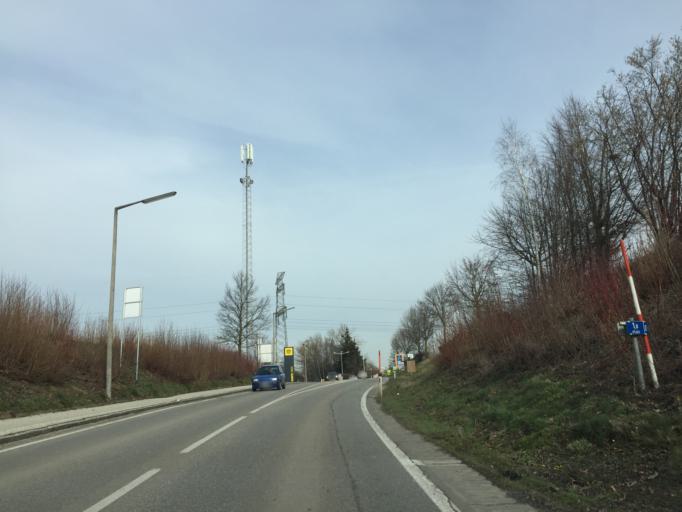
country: AT
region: Upper Austria
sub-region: Politischer Bezirk Ried im Innkreis
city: Ried im Innkreis
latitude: 48.2203
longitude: 13.4957
